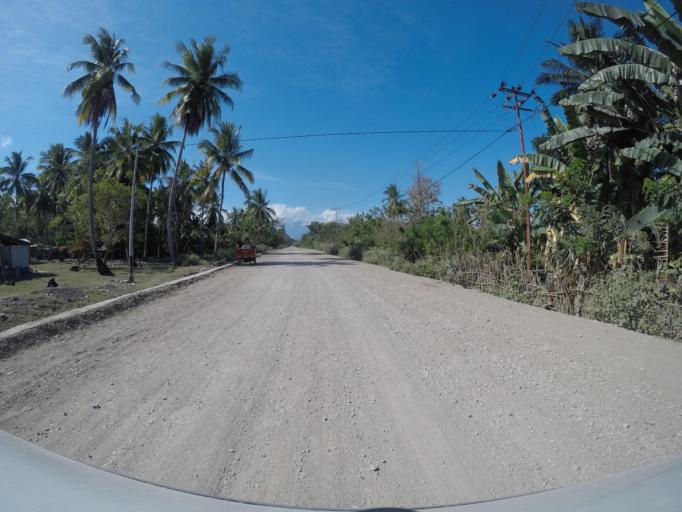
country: TL
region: Viqueque
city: Viqueque
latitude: -8.8597
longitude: 126.5096
